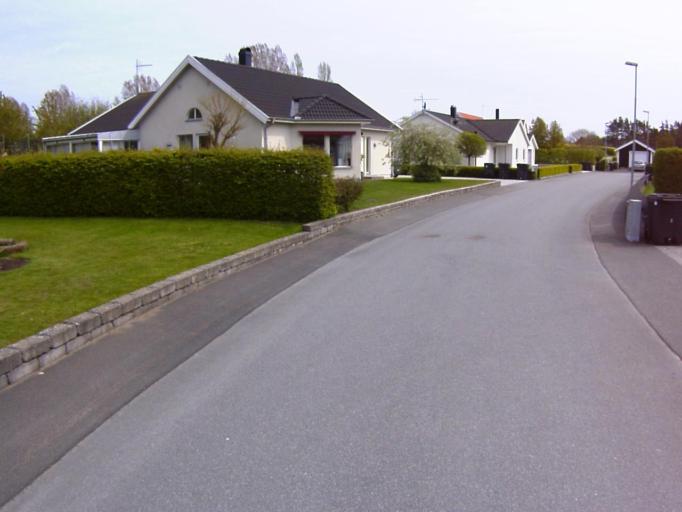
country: SE
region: Skane
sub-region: Kristianstads Kommun
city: Fjalkinge
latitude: 56.0795
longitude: 14.2163
